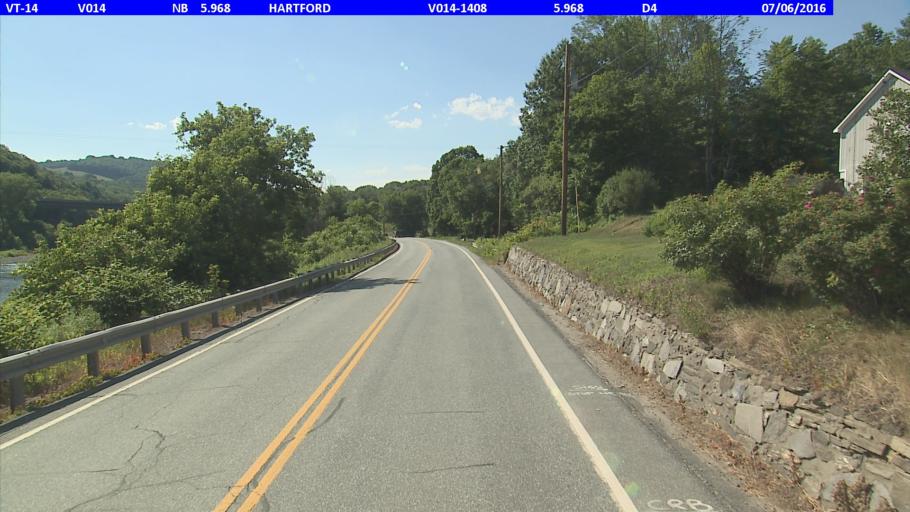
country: US
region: Vermont
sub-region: Windsor County
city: Wilder
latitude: 43.7022
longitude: -72.4068
